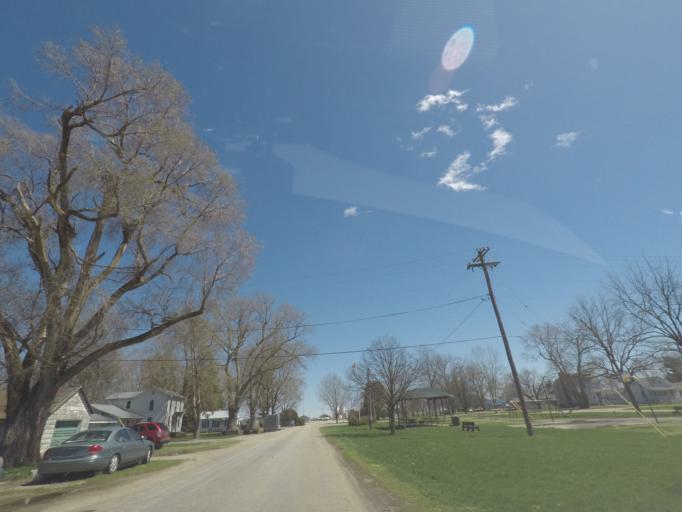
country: US
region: Illinois
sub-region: Logan County
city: Atlanta
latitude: 40.1435
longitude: -89.1928
